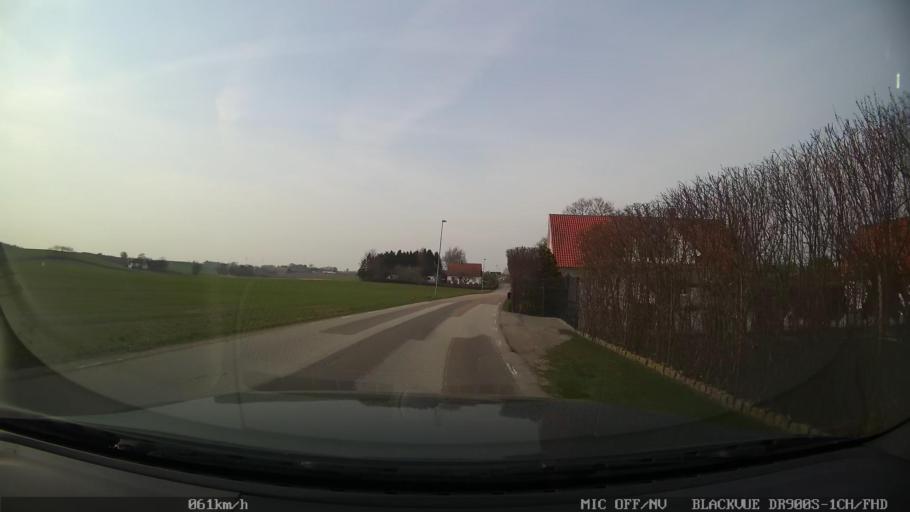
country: SE
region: Skane
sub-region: Ystads Kommun
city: Ystad
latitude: 55.4458
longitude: 13.8340
